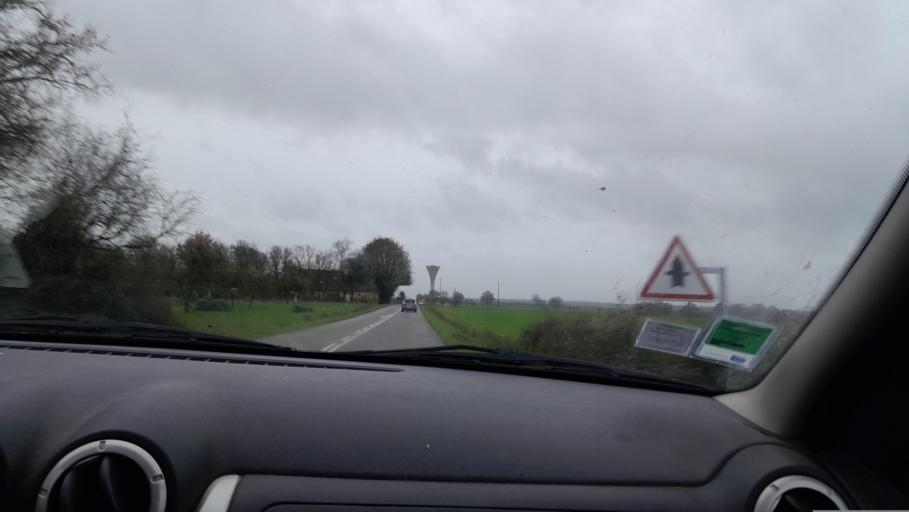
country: FR
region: Pays de la Loire
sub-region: Departement de la Mayenne
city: Ballots
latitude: 47.9210
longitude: -1.0958
